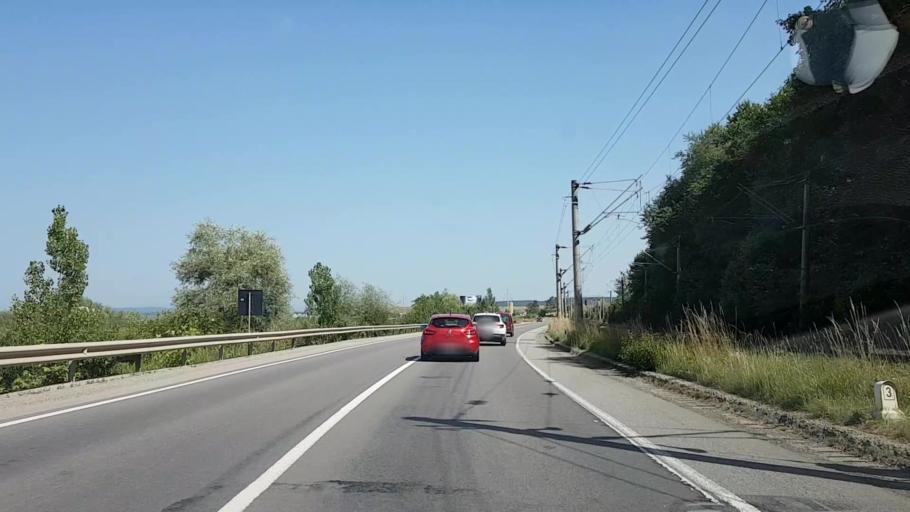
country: RO
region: Bistrita-Nasaud
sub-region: Comuna Beclean
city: Beclean
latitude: 47.1863
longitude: 24.2003
